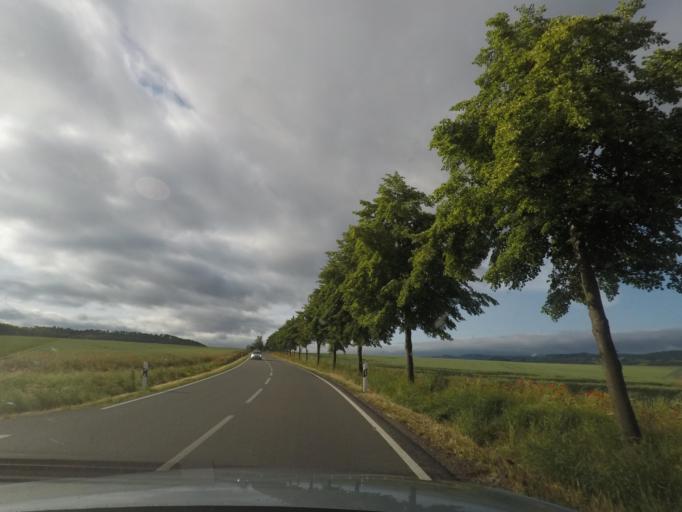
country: DE
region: Saxony-Anhalt
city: Derenburg
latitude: 51.8605
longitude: 10.9068
